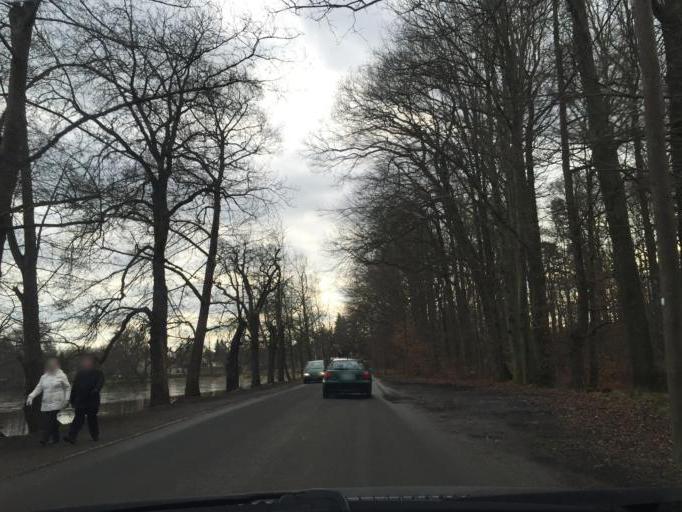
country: DE
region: Saxony
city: Moritzburg
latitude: 51.1681
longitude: 13.6727
